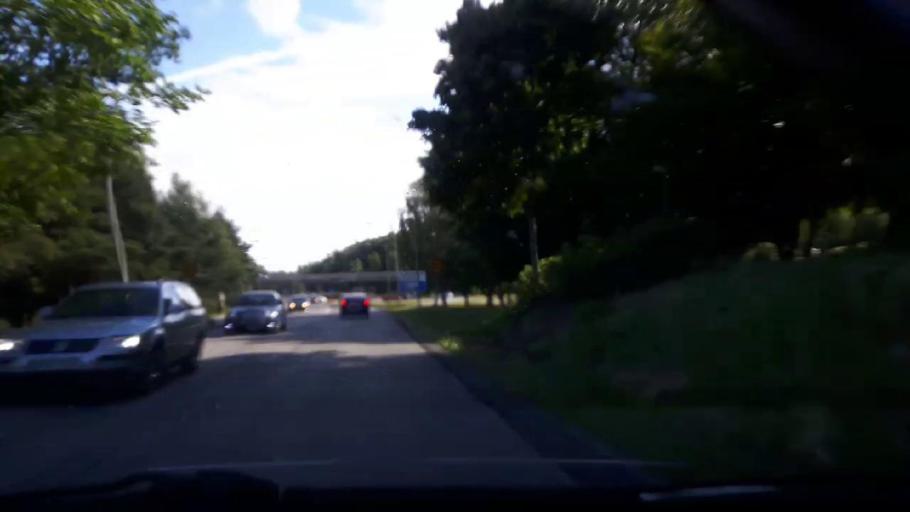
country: SE
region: Stockholm
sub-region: Sodertalje Kommun
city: Soedertaelje
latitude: 59.1781
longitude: 17.6328
